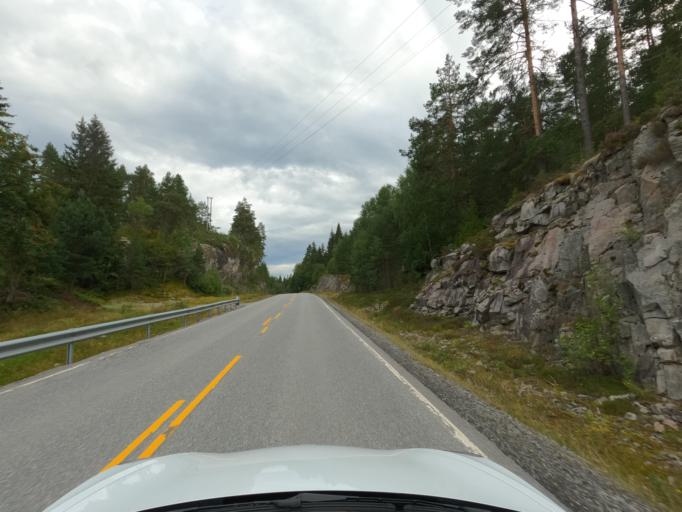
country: NO
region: Telemark
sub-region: Hjartdal
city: Sauland
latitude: 59.7424
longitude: 9.0203
